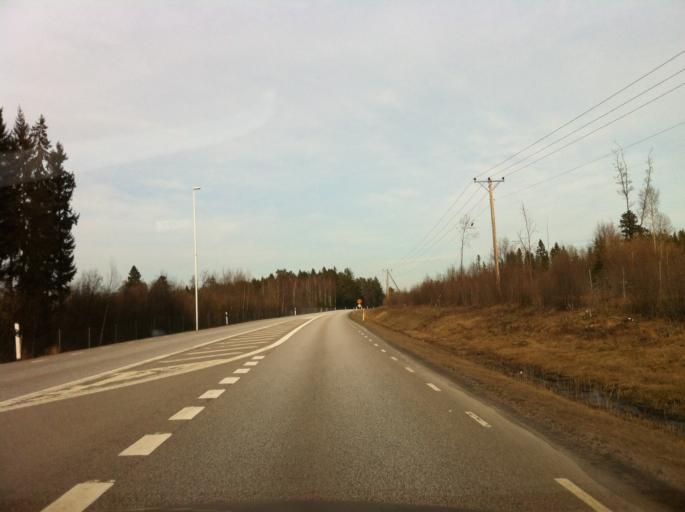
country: SE
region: Vaestra Goetaland
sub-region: Gullspangs Kommun
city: Gullspang
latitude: 58.9312
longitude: 14.0343
